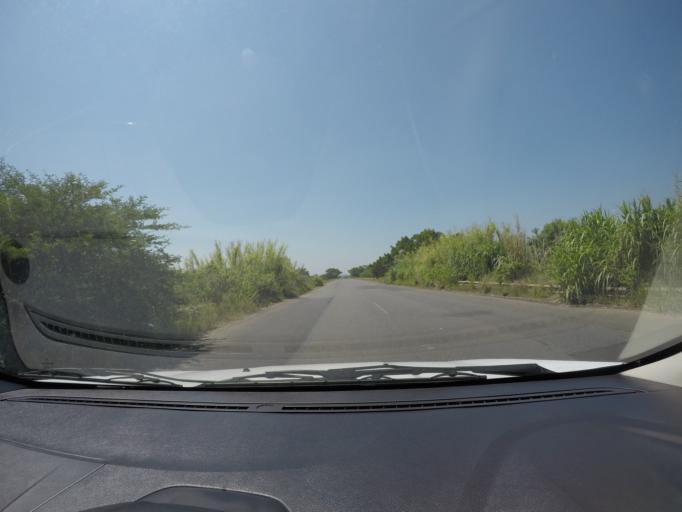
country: ZA
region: KwaZulu-Natal
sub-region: uThungulu District Municipality
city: Empangeni
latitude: -28.8008
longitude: 31.9584
